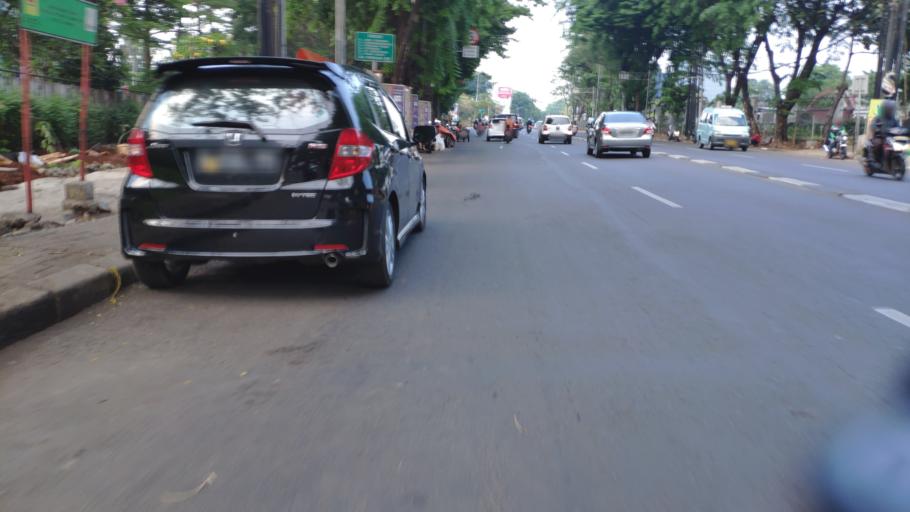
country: ID
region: Jakarta Raya
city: Jakarta
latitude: -6.2939
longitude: 106.8161
